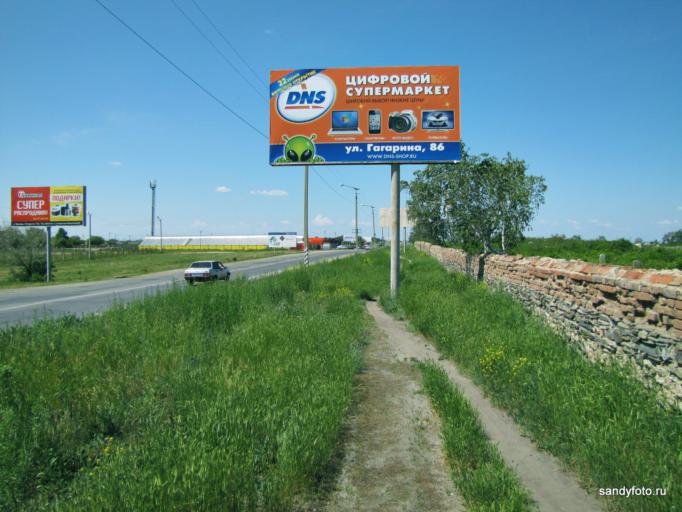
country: RU
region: Chelyabinsk
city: Troitsk
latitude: 54.0808
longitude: 61.5284
